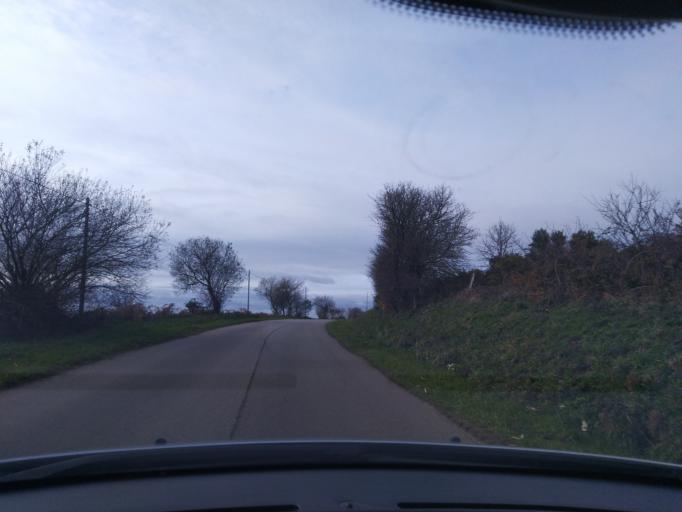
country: FR
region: Brittany
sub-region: Departement du Finistere
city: Guerlesquin
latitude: 48.5236
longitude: -3.6004
